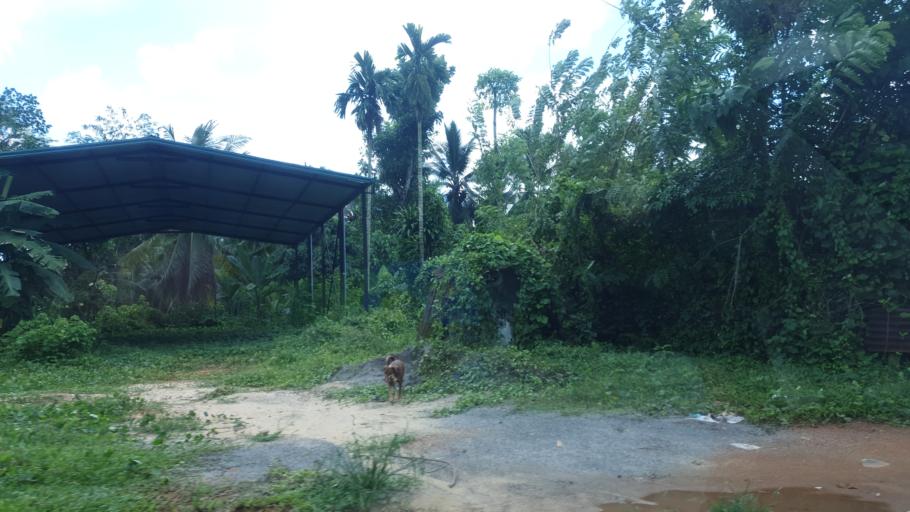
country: LK
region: Western
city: Horawala Junction
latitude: 6.5337
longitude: 80.1376
